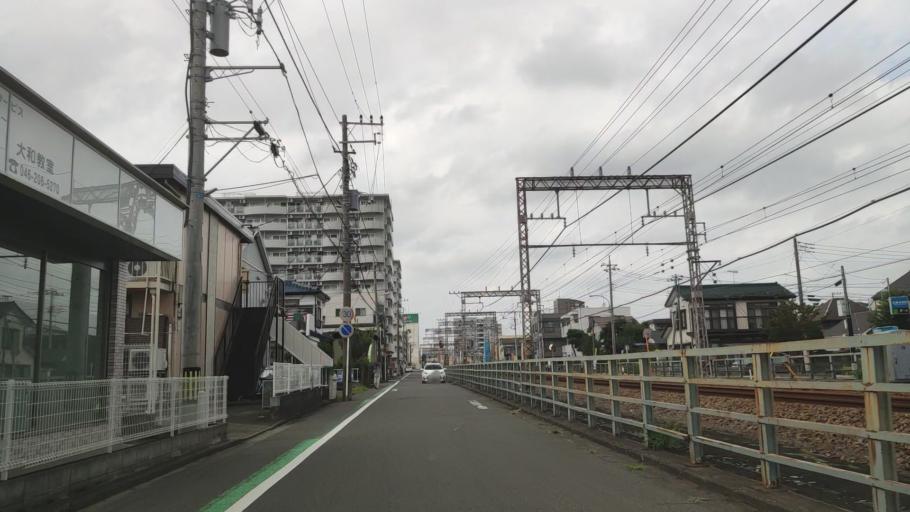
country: JP
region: Kanagawa
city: Minami-rinkan
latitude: 35.4857
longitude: 139.4531
